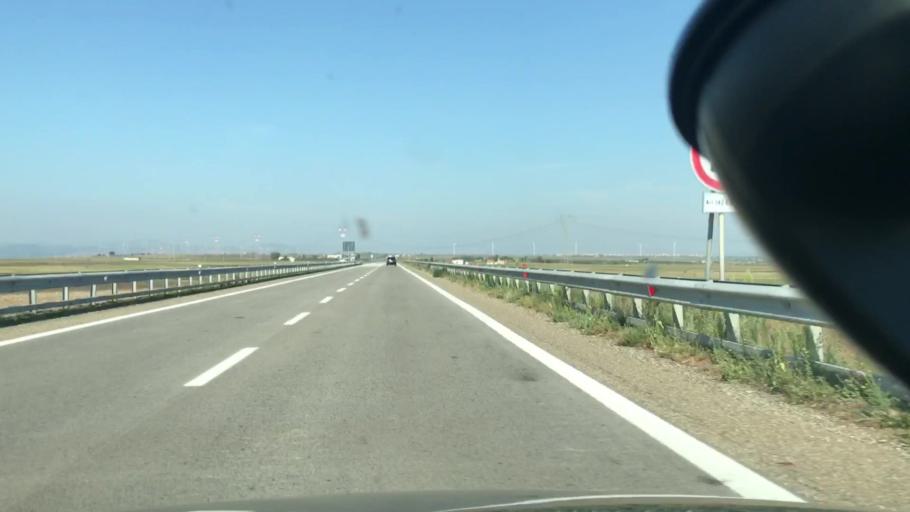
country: IT
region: Basilicate
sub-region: Provincia di Potenza
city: Venosa
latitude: 40.9950
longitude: 15.8835
